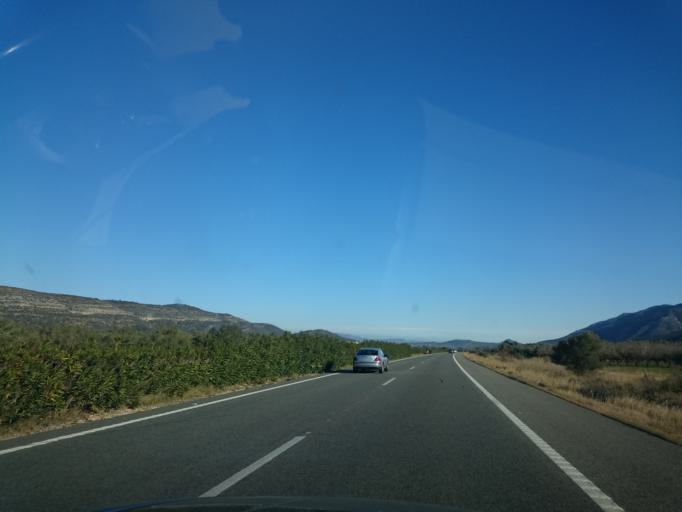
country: ES
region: Catalonia
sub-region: Provincia de Tarragona
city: Ulldecona
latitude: 40.6156
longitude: 0.4807
